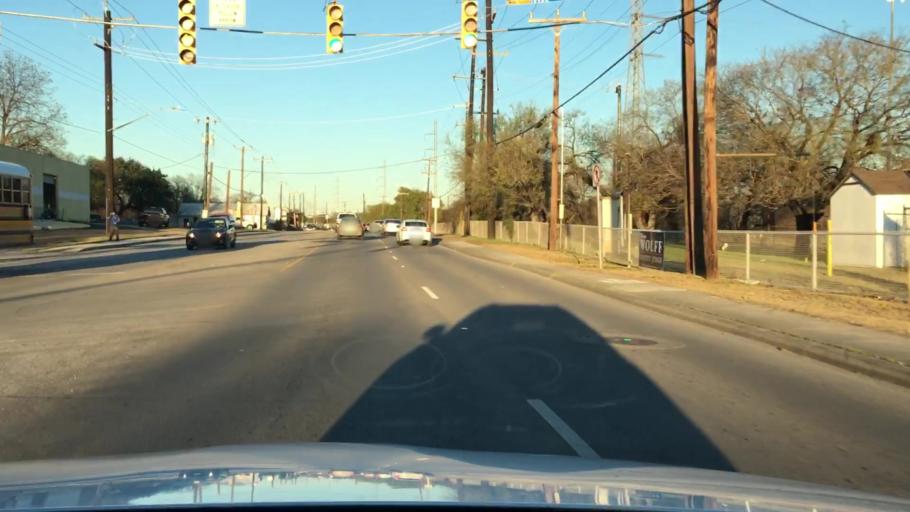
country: US
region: Texas
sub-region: Bexar County
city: Windcrest
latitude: 29.5353
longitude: -98.4274
